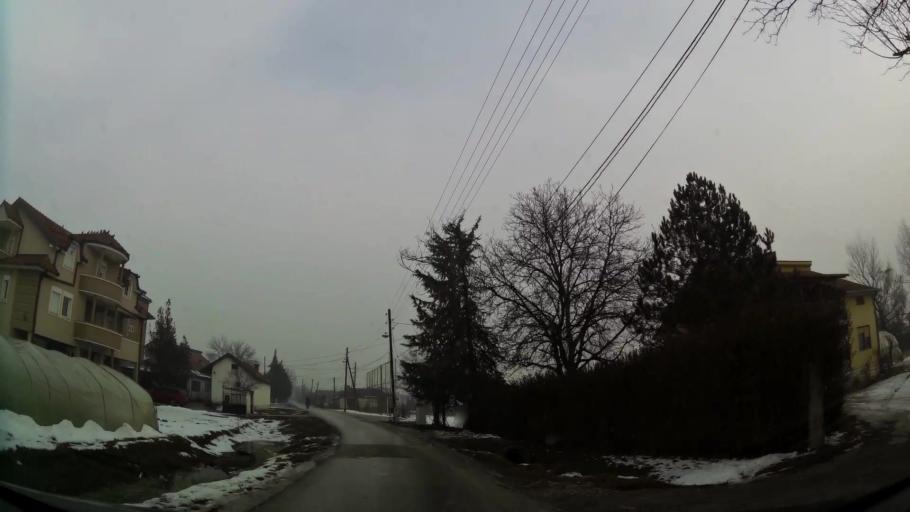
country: MK
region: Ilinden
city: Idrizovo
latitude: 41.9599
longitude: 21.5744
